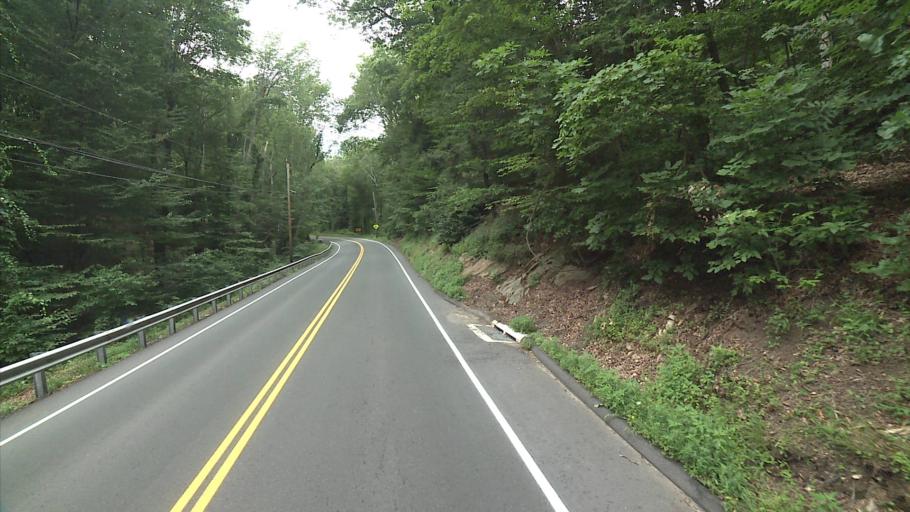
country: US
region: Connecticut
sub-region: New Haven County
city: Heritage Village
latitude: 41.5162
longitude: -73.2565
